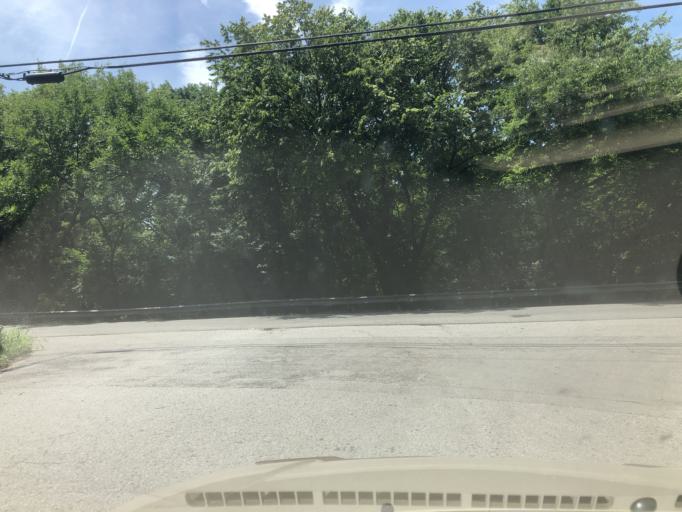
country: US
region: Tennessee
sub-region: Davidson County
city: Lakewood
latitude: 36.2514
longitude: -86.6906
